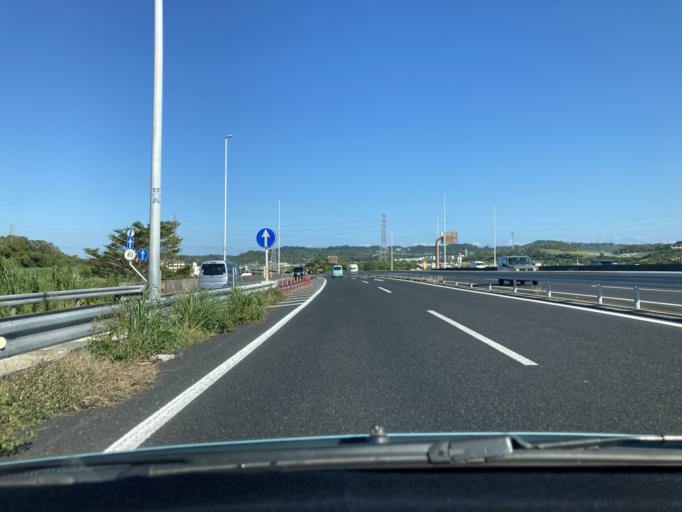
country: JP
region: Okinawa
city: Tomigusuku
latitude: 26.1809
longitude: 127.7272
